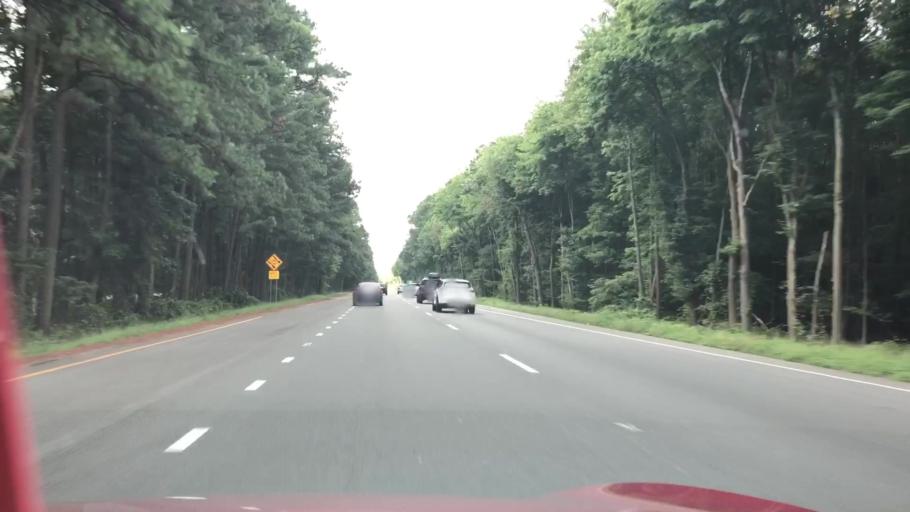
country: US
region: Maryland
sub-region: Somerset County
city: Princess Anne
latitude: 38.1519
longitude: -75.6946
